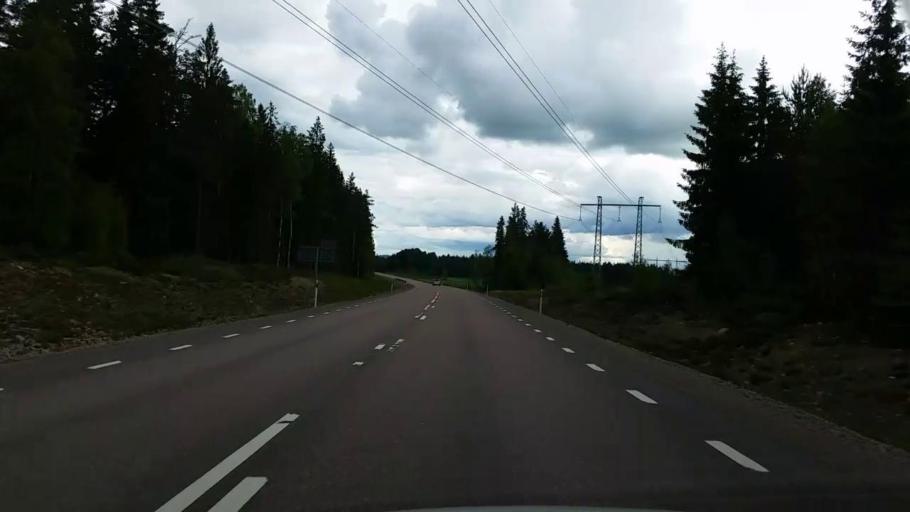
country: SE
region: Dalarna
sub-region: Avesta Kommun
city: Horndal
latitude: 60.4722
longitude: 16.4484
